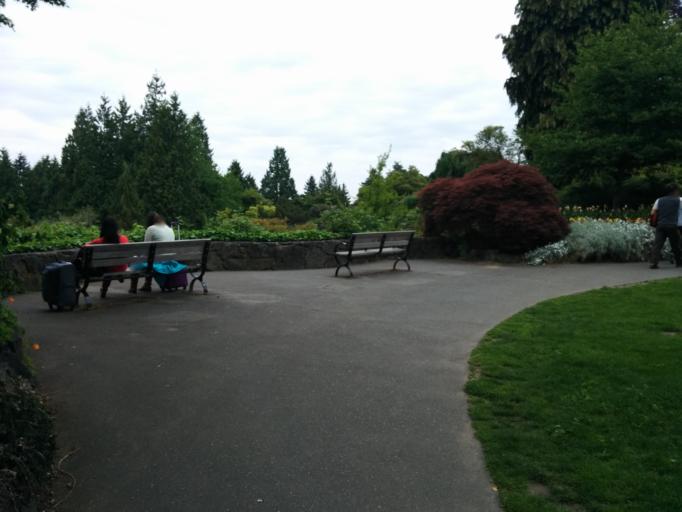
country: CA
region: British Columbia
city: Vancouver
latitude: 49.2420
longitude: -123.1150
